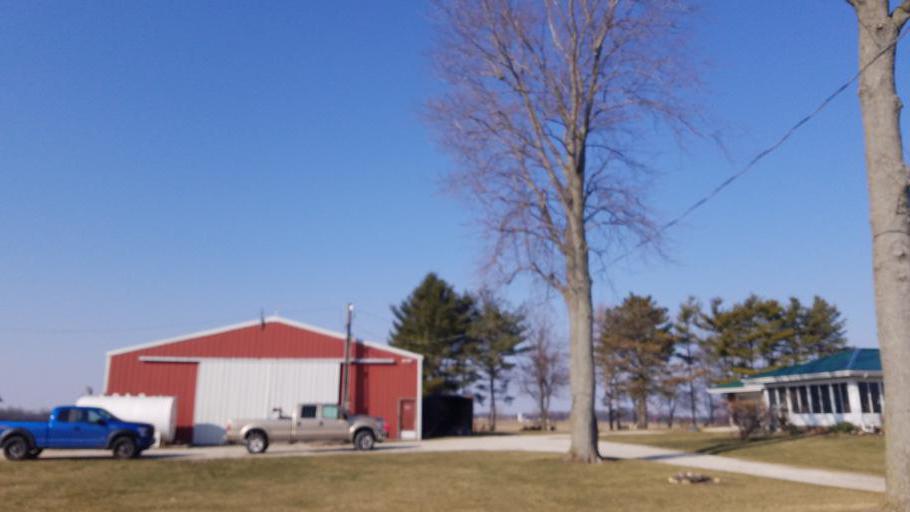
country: US
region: Ohio
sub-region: Morrow County
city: Mount Gilead
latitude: 40.6440
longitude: -82.8598
